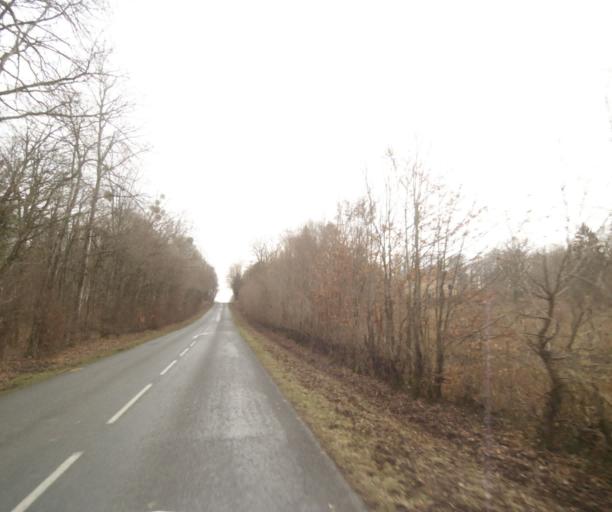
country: FR
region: Champagne-Ardenne
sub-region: Departement de la Haute-Marne
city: Villiers-en-Lieu
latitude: 48.7181
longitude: 4.8794
